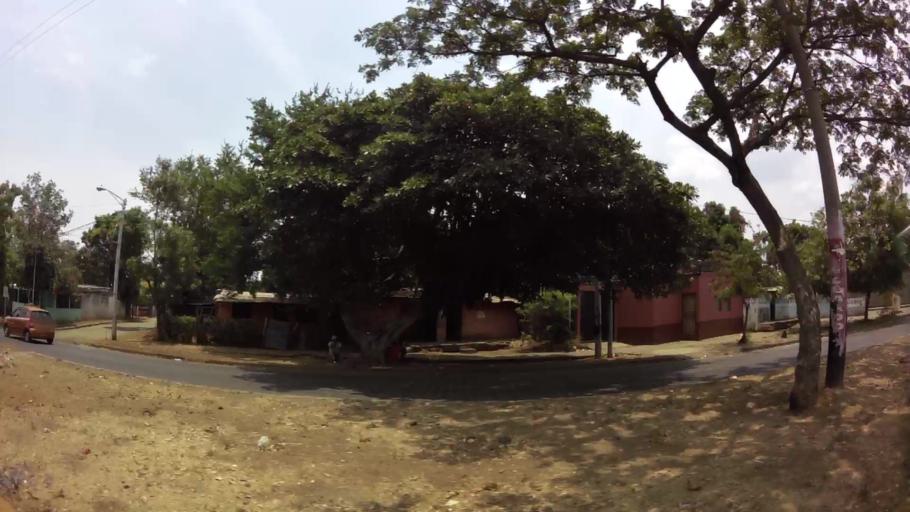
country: NI
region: Managua
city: Managua
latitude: 12.1289
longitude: -86.2913
